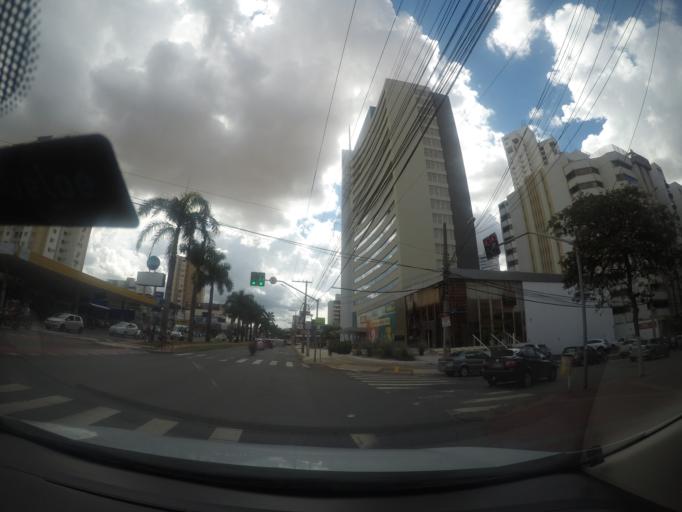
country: BR
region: Goias
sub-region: Goiania
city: Goiania
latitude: -16.7233
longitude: -49.2670
